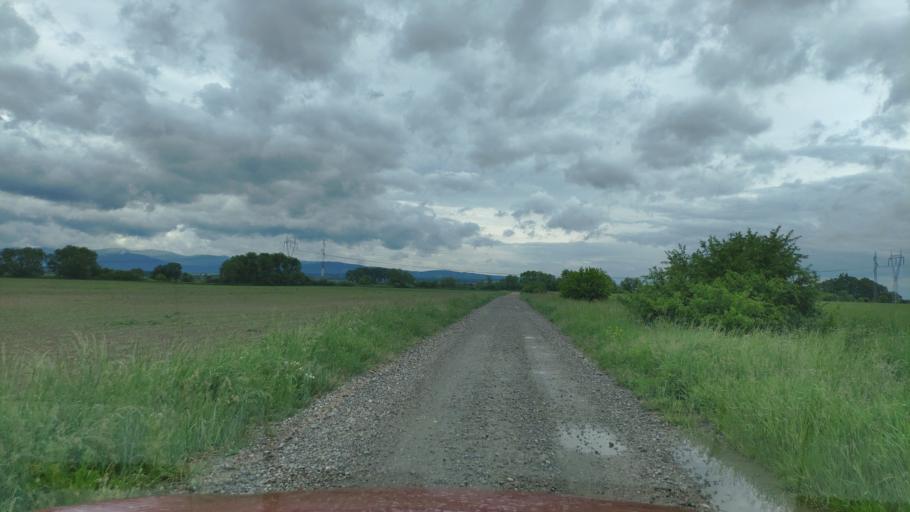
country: SK
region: Kosicky
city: Moldava nad Bodvou
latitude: 48.5582
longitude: 21.1159
